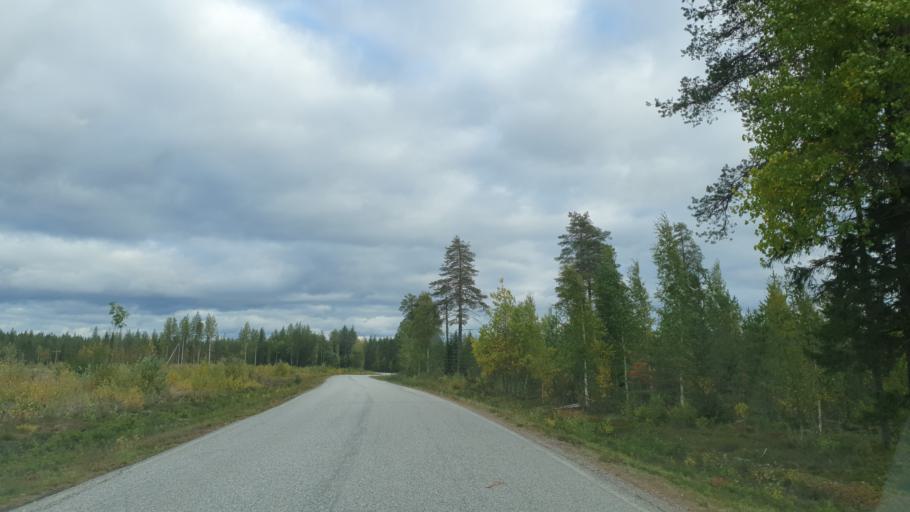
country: FI
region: Kainuu
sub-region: Kehys-Kainuu
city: Kuhmo
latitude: 63.9493
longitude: 29.7564
